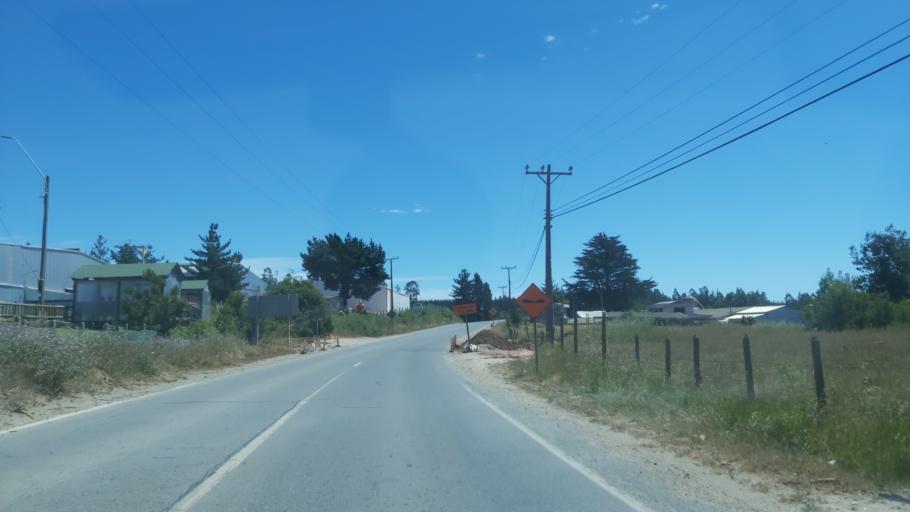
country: CL
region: Maule
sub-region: Provincia de Talca
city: Constitucion
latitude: -35.3746
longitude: -72.4172
